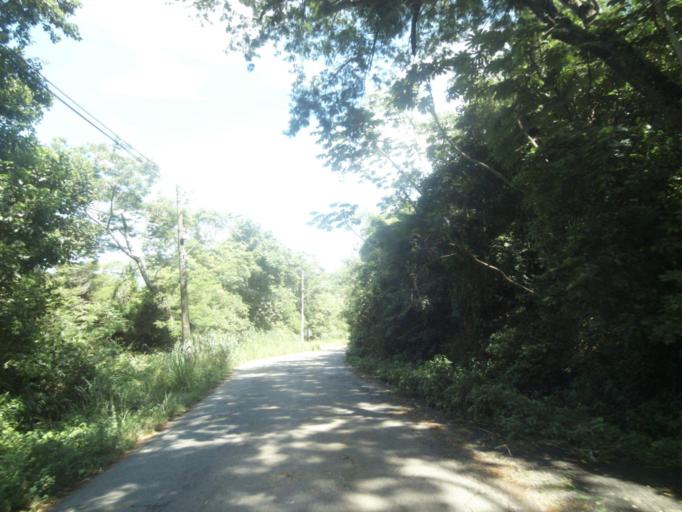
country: BR
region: Rio de Janeiro
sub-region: Niteroi
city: Niteroi
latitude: -22.9632
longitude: -43.0243
